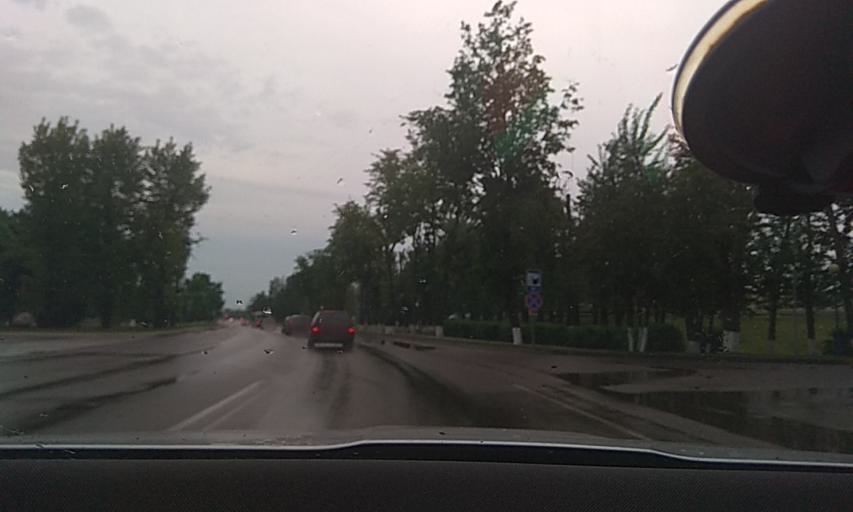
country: BY
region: Grodnenskaya
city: Hrodna
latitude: 53.6768
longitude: 23.8892
